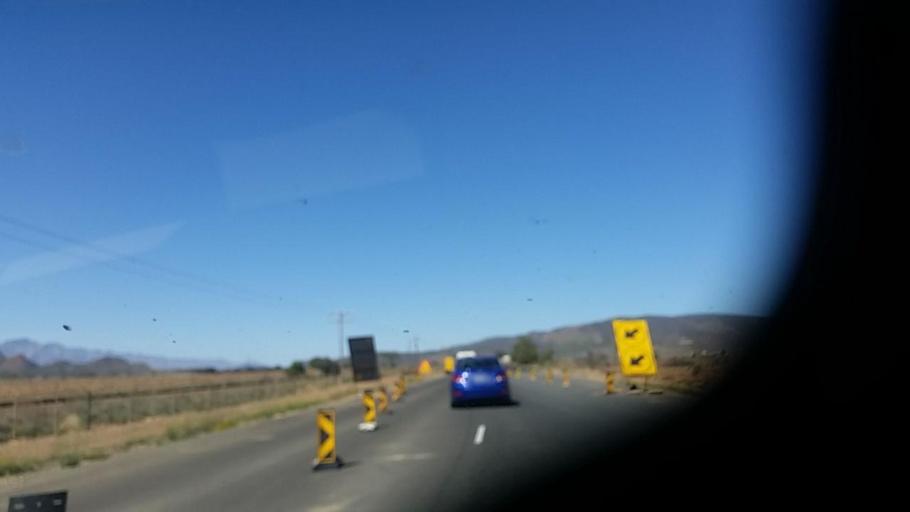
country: ZA
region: Western Cape
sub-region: Eden District Municipality
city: Oudtshoorn
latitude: -33.5611
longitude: 22.3964
